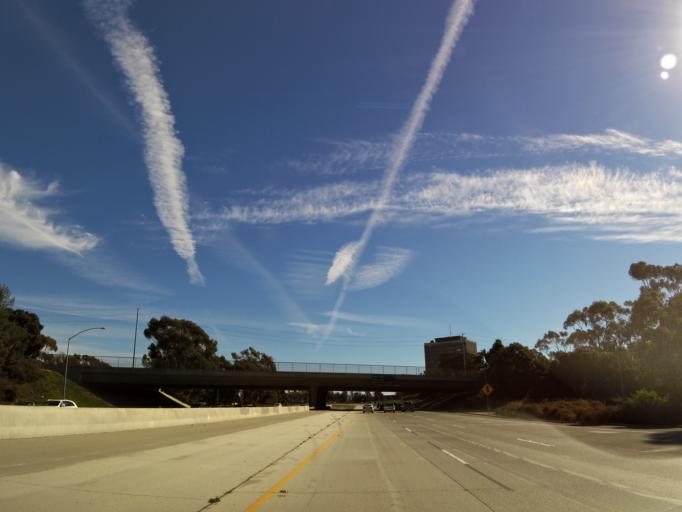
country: US
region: California
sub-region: Ventura County
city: El Rio
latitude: 34.2328
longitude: -119.1742
